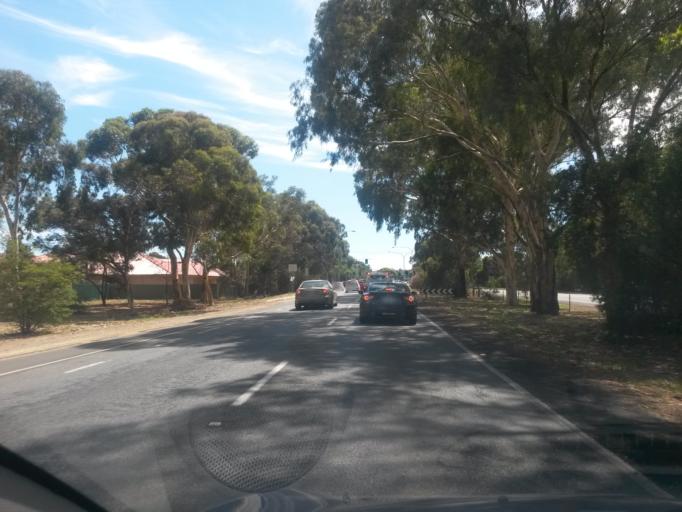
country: AU
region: South Australia
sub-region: Salisbury
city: Salisbury
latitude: -34.7844
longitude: 138.6532
